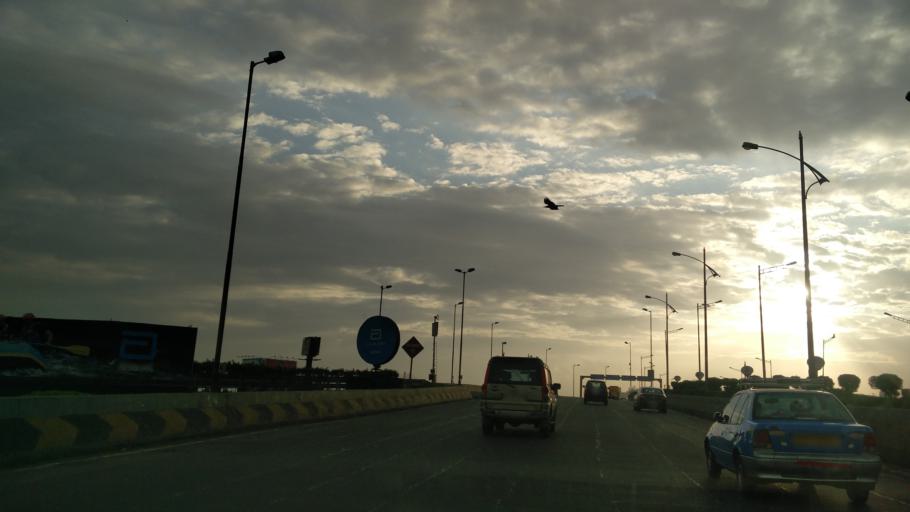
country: IN
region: Maharashtra
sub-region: Mumbai Suburban
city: Mumbai
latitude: 19.0504
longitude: 72.8397
